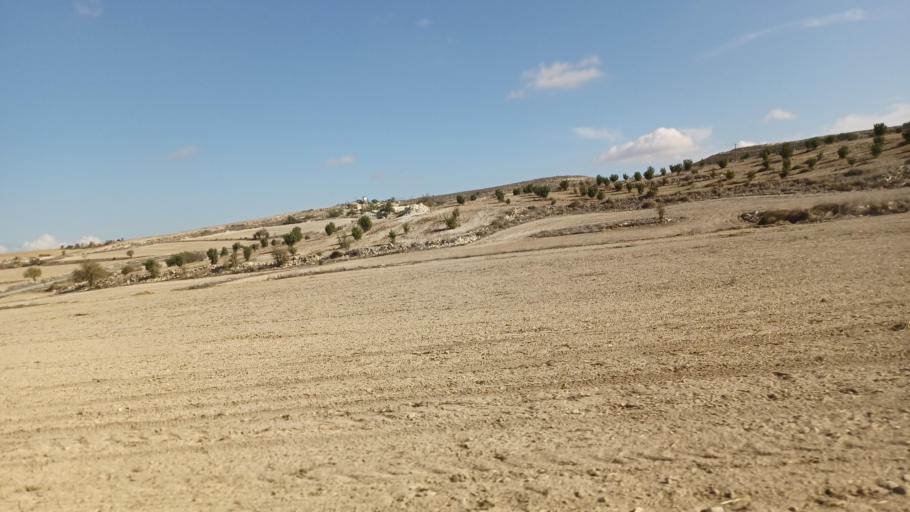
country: CY
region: Larnaka
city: Troulloi
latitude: 35.0339
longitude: 33.5746
